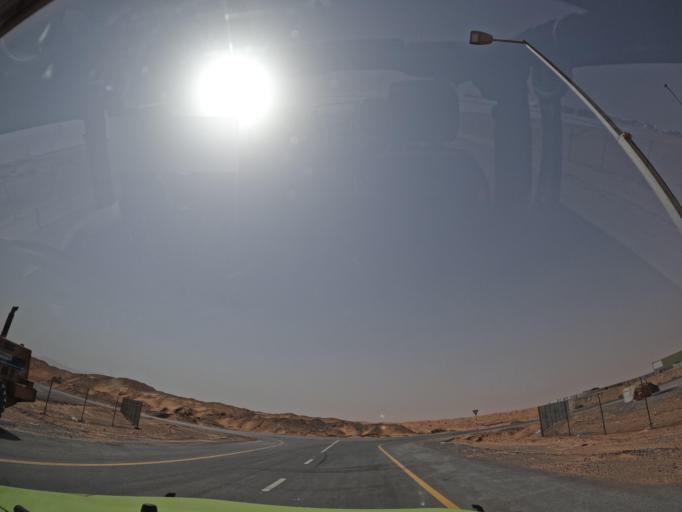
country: OM
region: Al Buraimi
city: Al Buraymi
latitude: 24.7391
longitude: 55.7980
